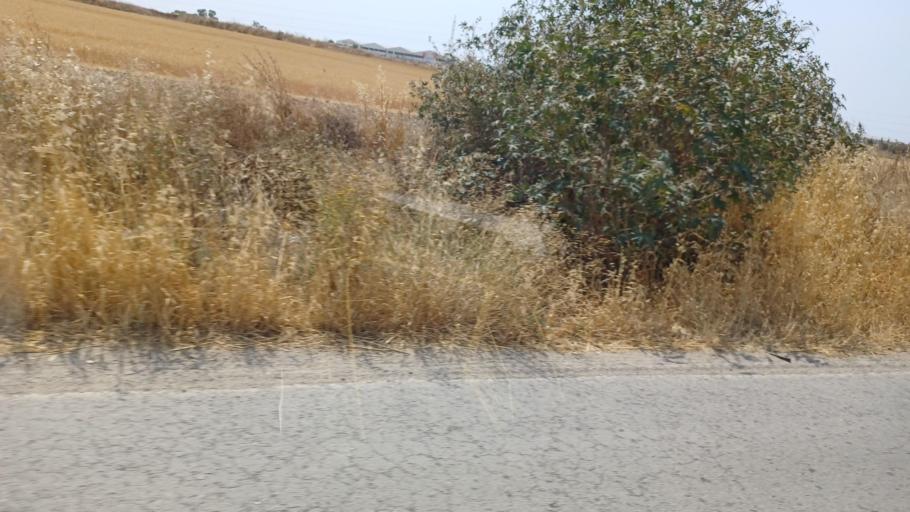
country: CY
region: Larnaka
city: Livadia
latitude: 34.9624
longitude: 33.6101
